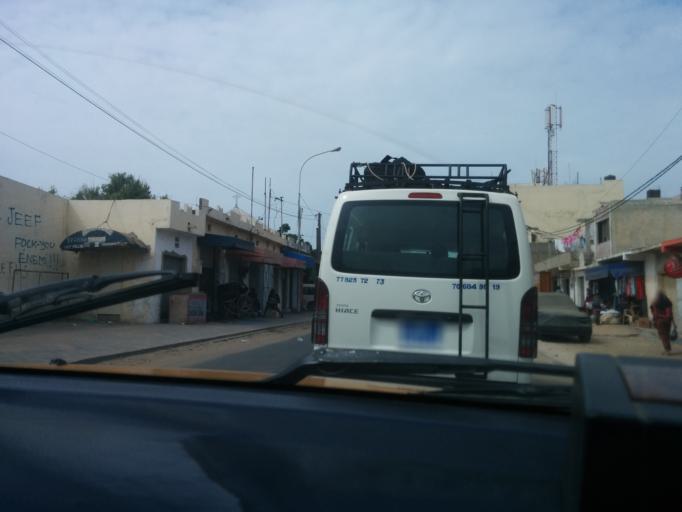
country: SN
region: Dakar
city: Pikine
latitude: 14.7582
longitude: -17.4363
